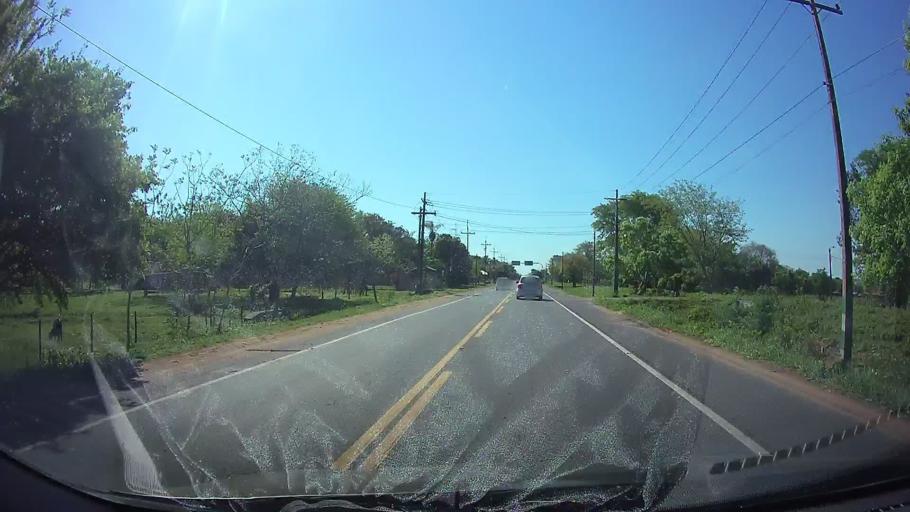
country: PY
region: Central
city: Ypacarai
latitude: -25.3923
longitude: -57.2944
